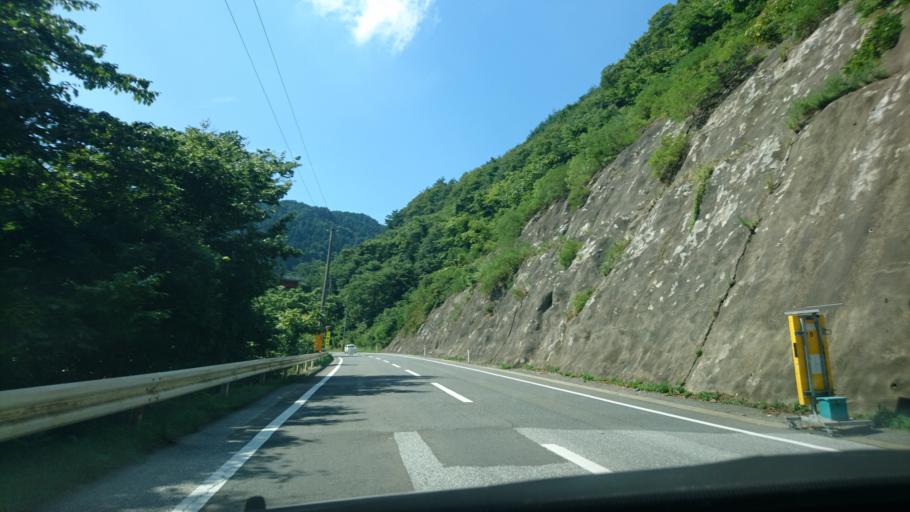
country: JP
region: Iwate
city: Ofunato
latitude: 39.0113
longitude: 141.4766
